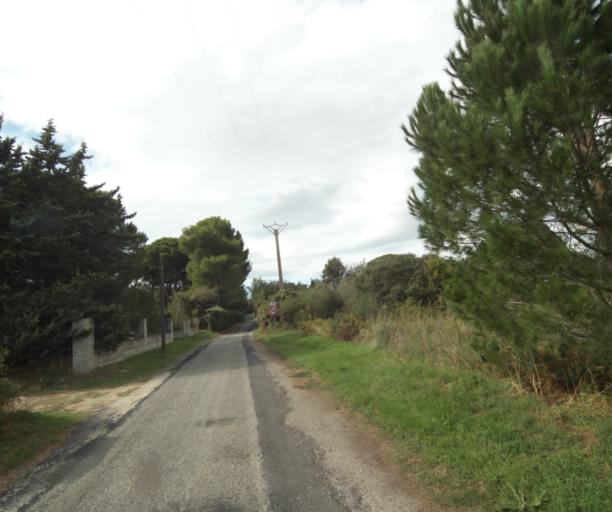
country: FR
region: Languedoc-Roussillon
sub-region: Departement des Pyrenees-Orientales
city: Argelers
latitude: 42.5436
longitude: 3.0039
